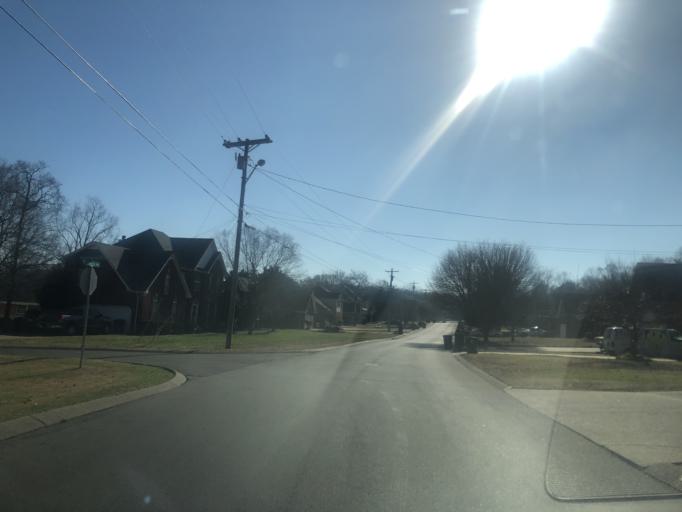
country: US
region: Tennessee
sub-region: Rutherford County
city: Smyrna
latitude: 35.9753
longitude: -86.5420
